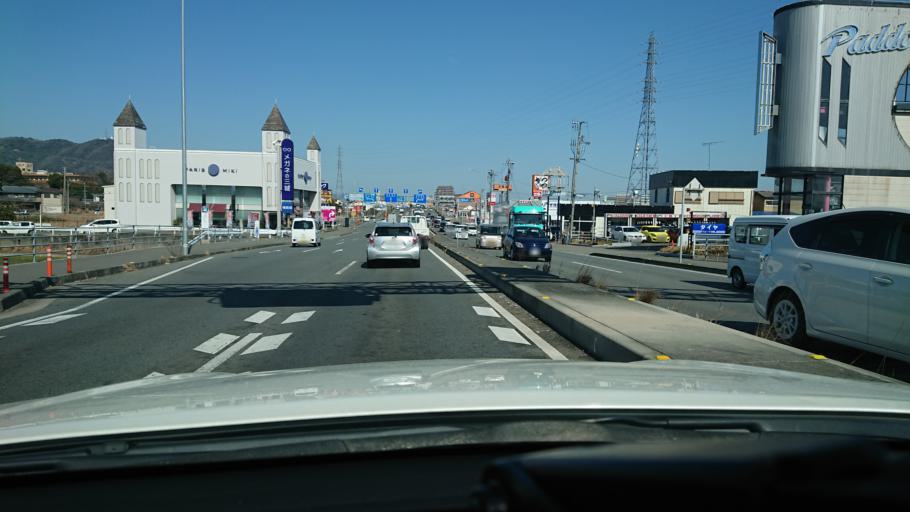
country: JP
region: Tokushima
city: Tokushima-shi
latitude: 34.0409
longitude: 134.5520
